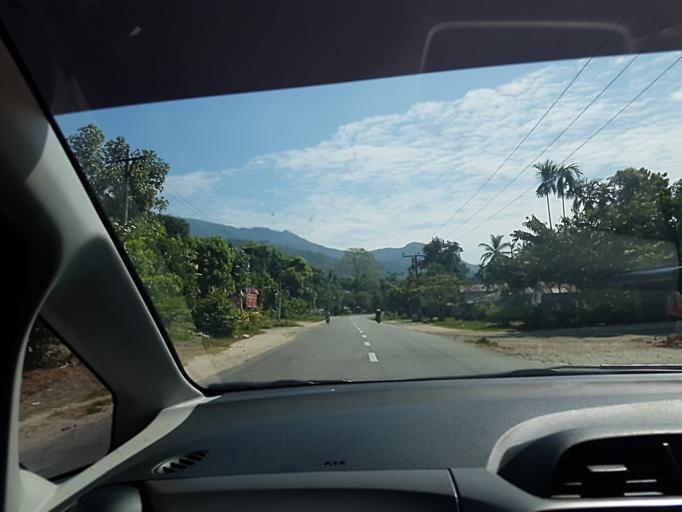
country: MM
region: Mon
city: Thaton
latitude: 16.7135
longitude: 97.4203
